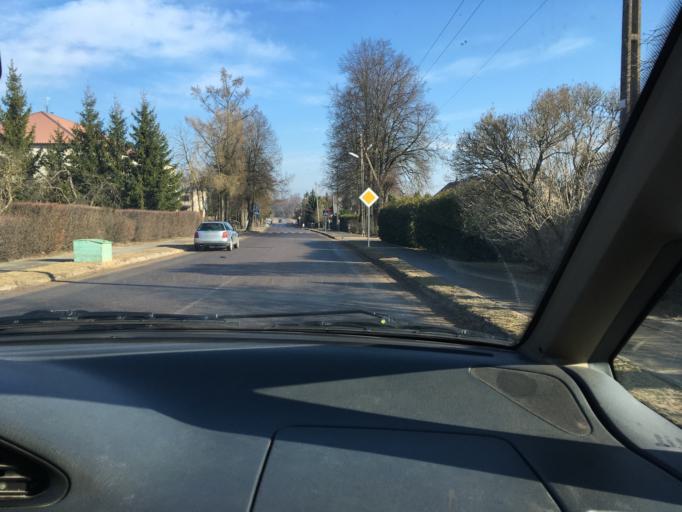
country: LT
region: Utenos apskritis
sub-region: Utena
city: Utena
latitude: 55.7370
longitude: 25.8331
